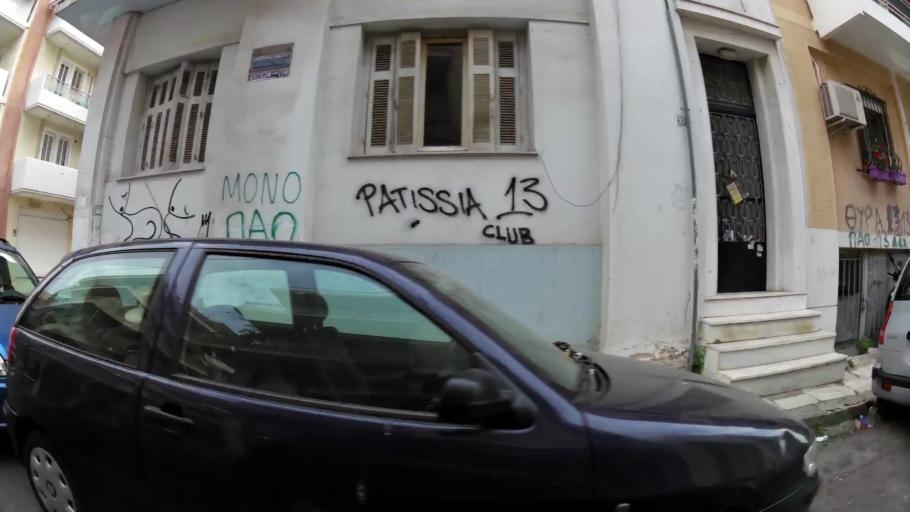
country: GR
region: Attica
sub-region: Nomarchia Athinas
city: Kipseli
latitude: 38.0108
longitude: 23.7259
